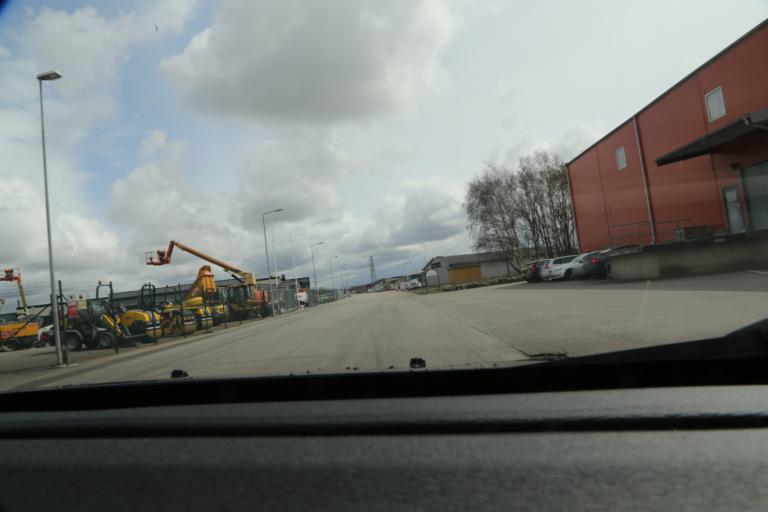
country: SE
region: Halland
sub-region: Varbergs Kommun
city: Varberg
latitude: 57.1243
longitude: 12.2800
